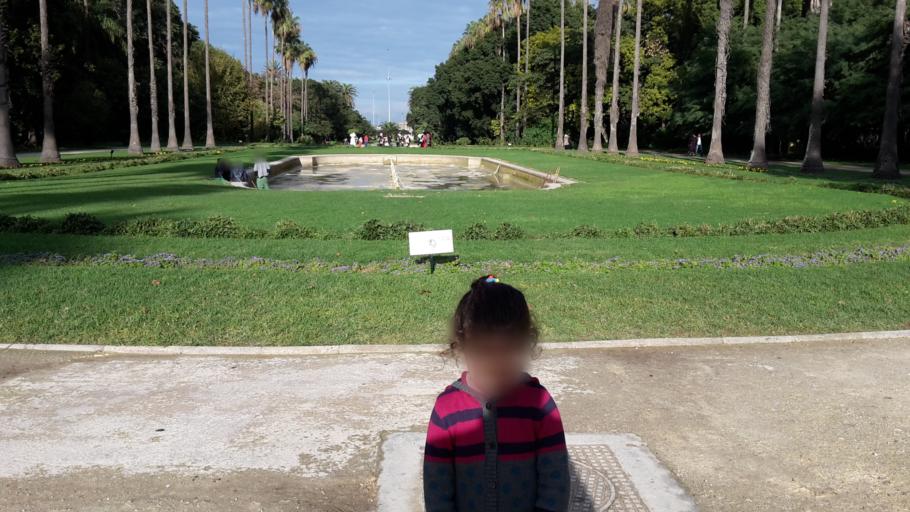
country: DZ
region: Alger
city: Algiers
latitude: 36.7494
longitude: 3.0744
